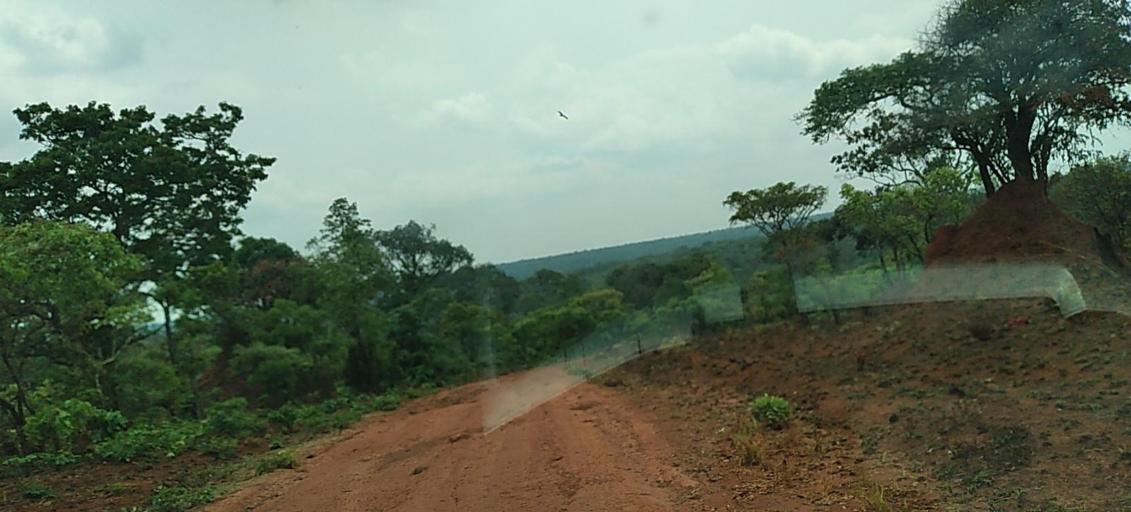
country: ZM
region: North-Western
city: Mwinilunga
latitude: -11.5142
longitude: 24.7889
